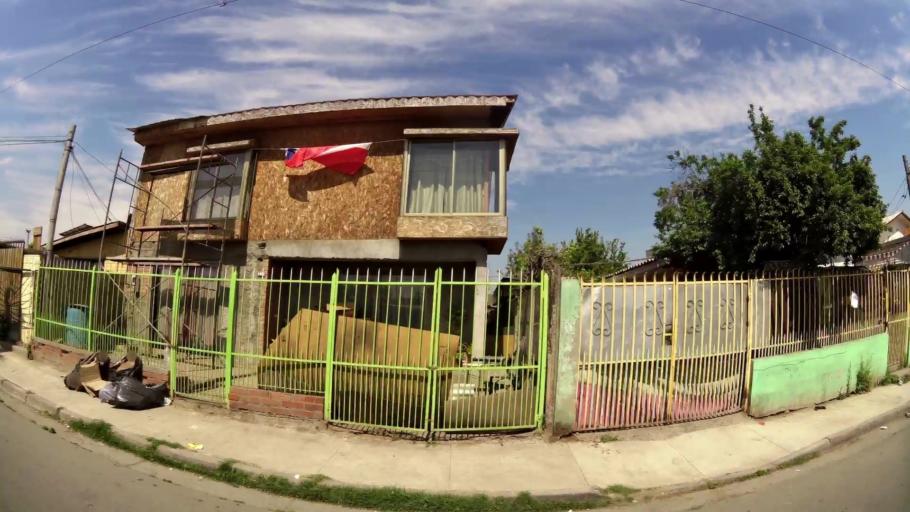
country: CL
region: Santiago Metropolitan
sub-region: Provincia de Santiago
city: La Pintana
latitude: -33.5472
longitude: -70.6479
